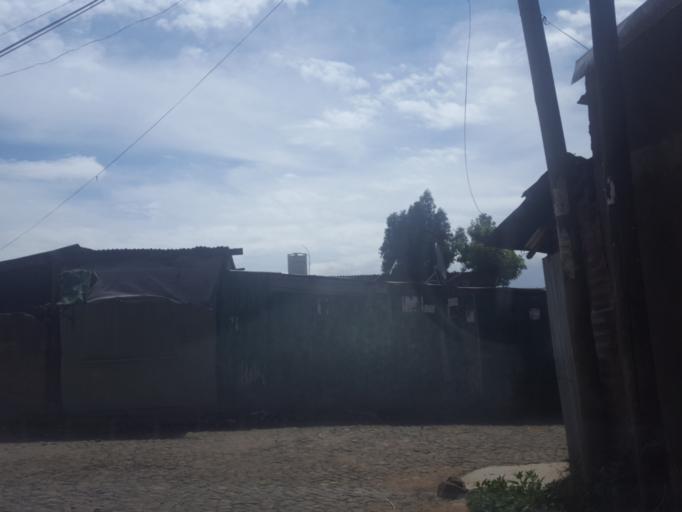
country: ET
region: Adis Abeba
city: Addis Ababa
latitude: 9.0649
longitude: 38.7425
